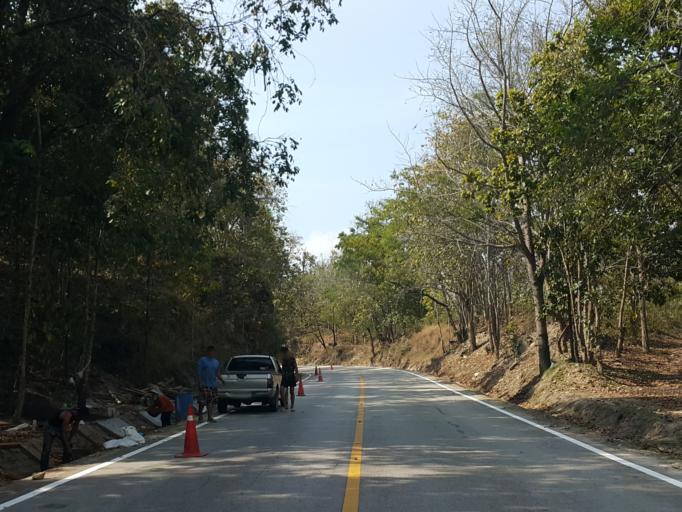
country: TH
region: Chiang Mai
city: Hot
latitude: 18.1736
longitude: 98.4471
